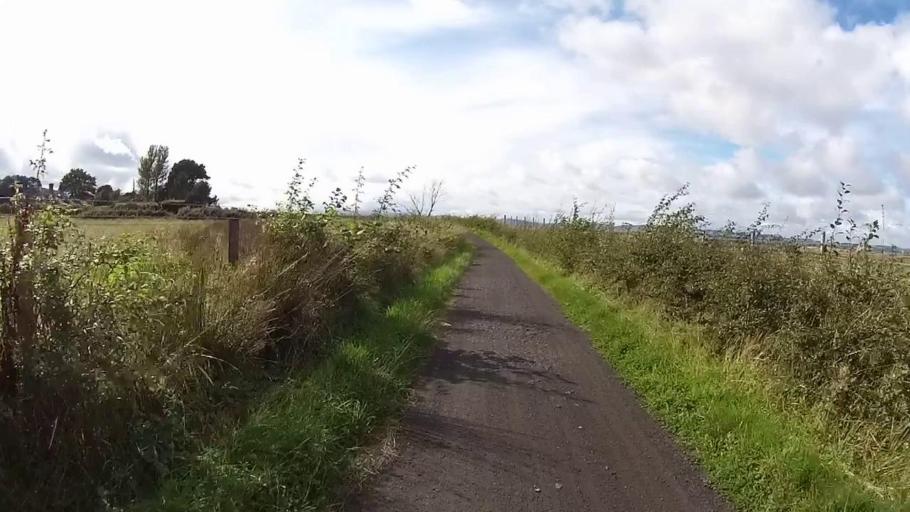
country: GB
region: Scotland
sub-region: Fife
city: Ballingry
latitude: 56.1730
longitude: -3.3694
